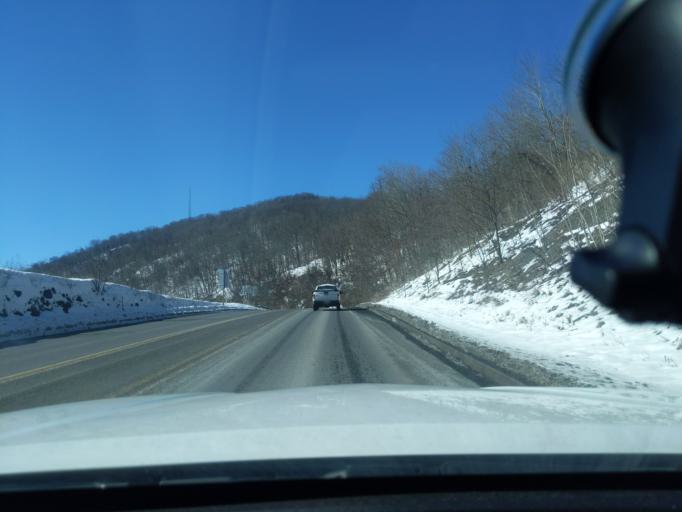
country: US
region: Maryland
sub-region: Allegany County
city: Westernport
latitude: 39.4841
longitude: -79.0484
